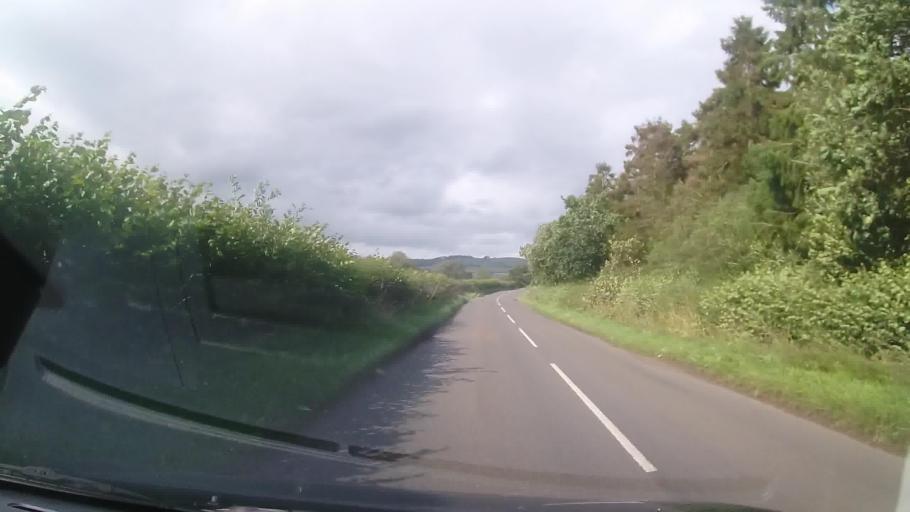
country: GB
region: England
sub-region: Shropshire
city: Lydham
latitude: 52.5083
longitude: -2.9667
